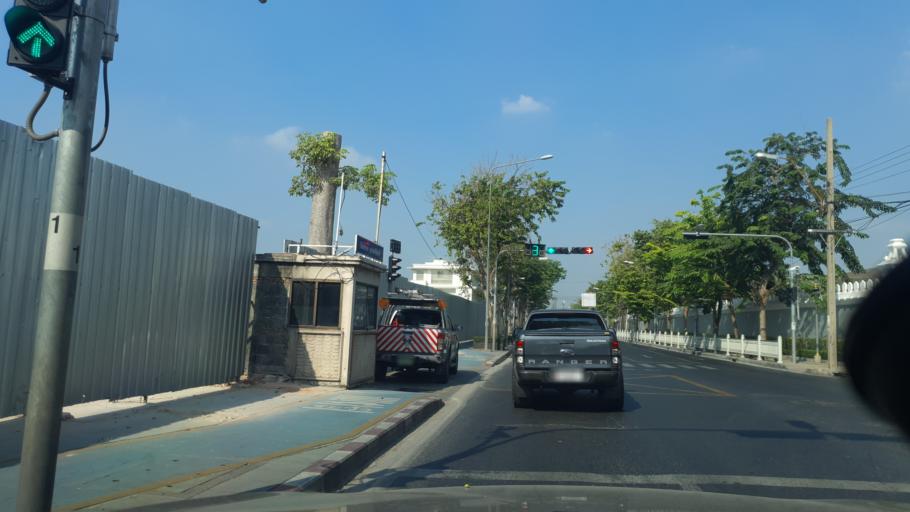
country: TH
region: Bangkok
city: Dusit
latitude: 13.7753
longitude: 100.5151
